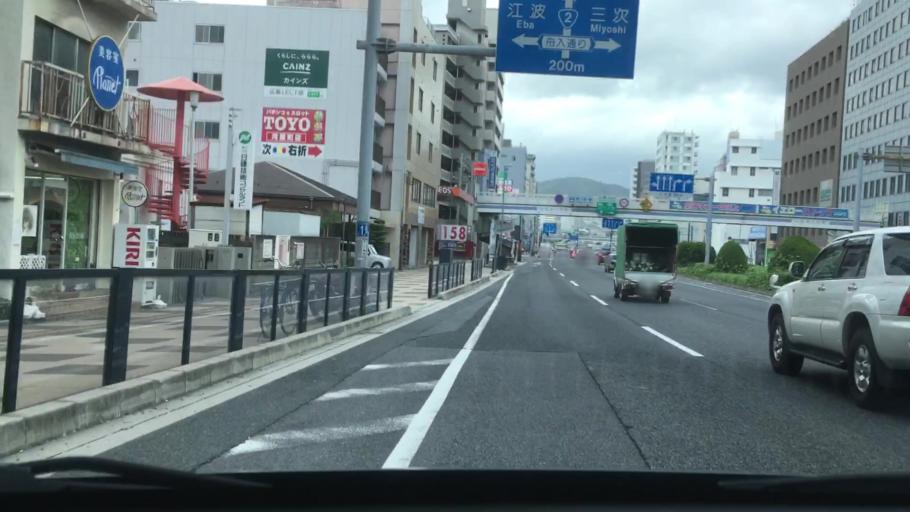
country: JP
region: Hiroshima
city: Hiroshima-shi
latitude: 34.3854
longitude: 132.4454
